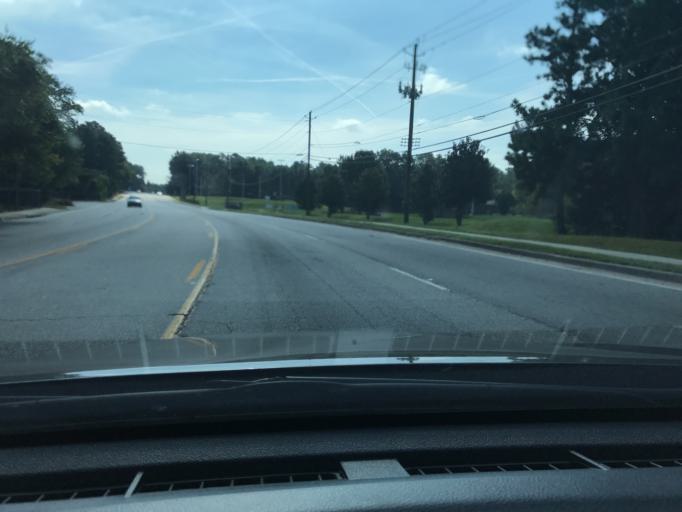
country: US
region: Georgia
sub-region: DeKalb County
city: Tucker
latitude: 33.8934
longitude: -84.2347
